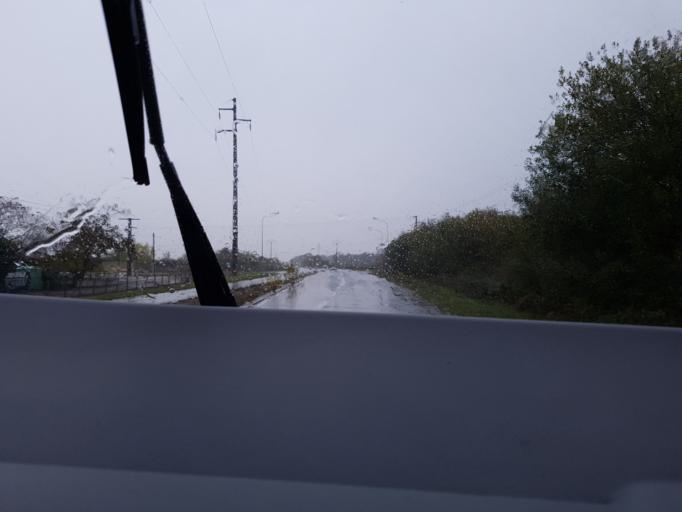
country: FR
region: Aquitaine
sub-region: Departement de la Gironde
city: Saint-Louis-de-Montferrand
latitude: 44.9533
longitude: -0.5180
